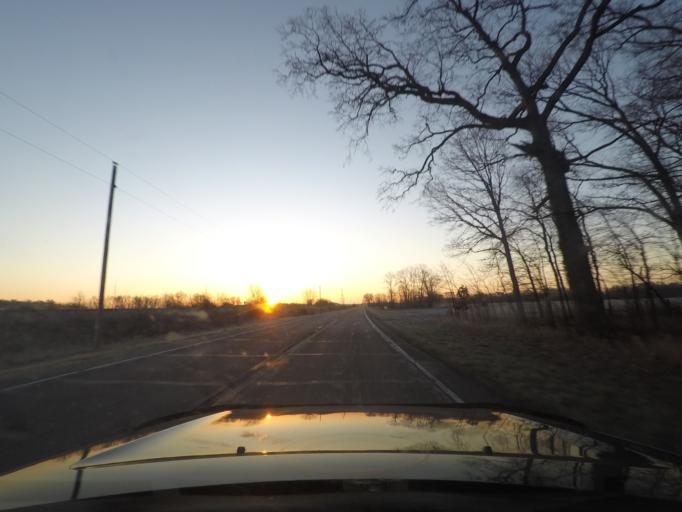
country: US
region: Indiana
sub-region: Saint Joseph County
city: Walkerton
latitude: 41.4762
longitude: -86.5449
